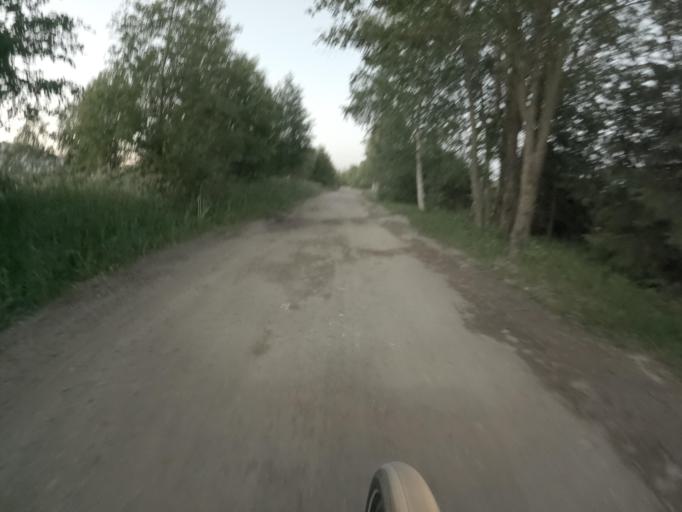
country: RU
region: St.-Petersburg
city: Sapernyy
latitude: 59.7793
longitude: 30.6695
